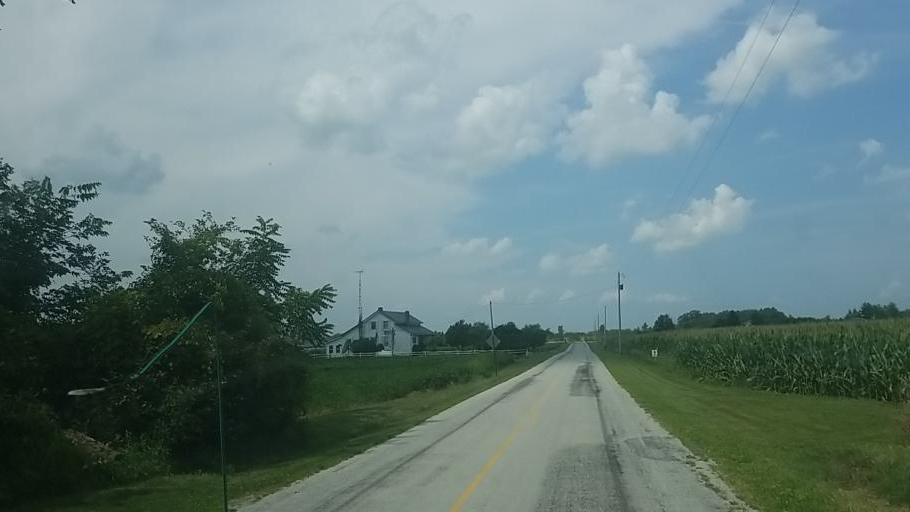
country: US
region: Ohio
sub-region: Hardin County
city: Kenton
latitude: 40.7493
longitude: -83.6024
